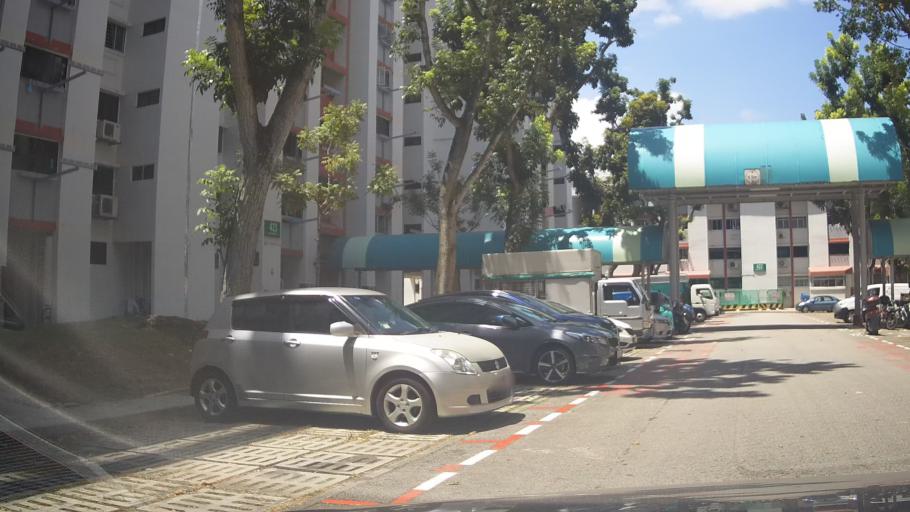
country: SG
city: Singapore
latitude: 1.3573
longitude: 103.9479
